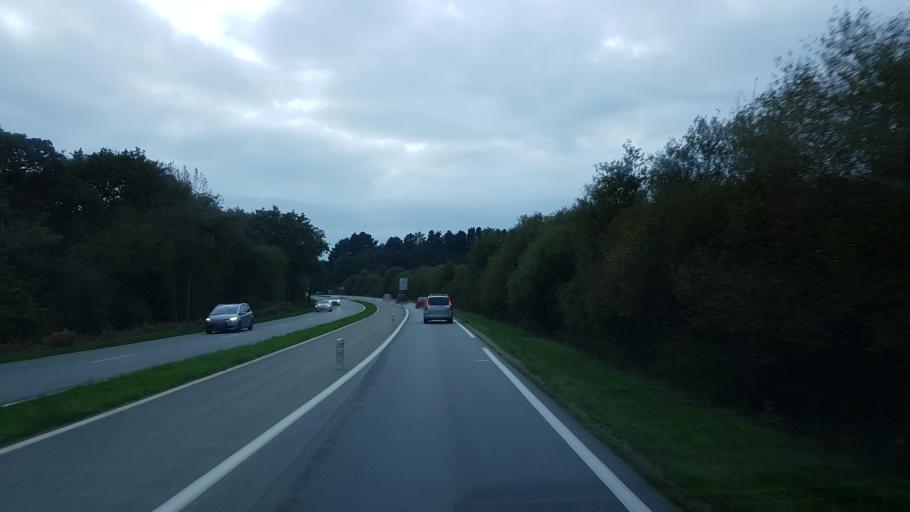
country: FR
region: Brittany
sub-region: Departement du Morbihan
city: Sarzeau
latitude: 47.5407
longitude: -2.7342
